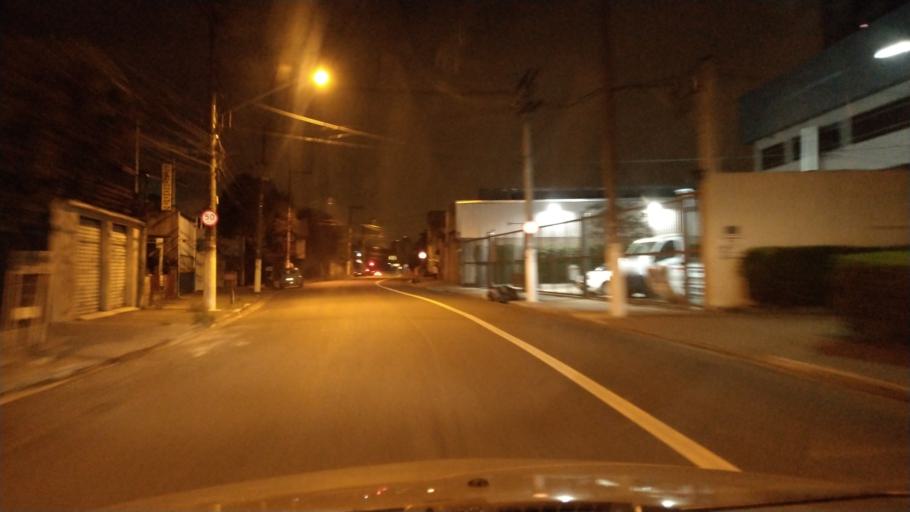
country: BR
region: Sao Paulo
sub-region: Sao Paulo
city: Sao Paulo
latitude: -23.5069
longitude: -46.6730
